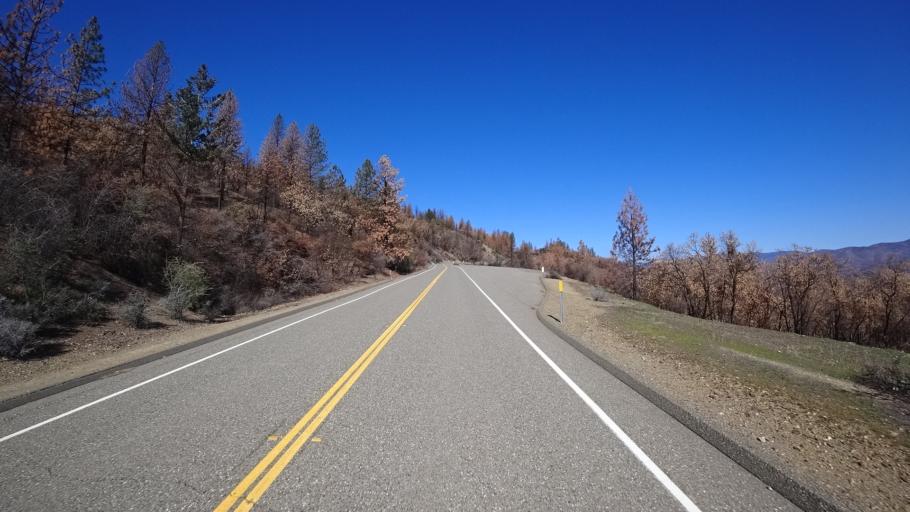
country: US
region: California
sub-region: Tehama County
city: Rancho Tehama Reserve
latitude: 39.6695
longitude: -122.6891
